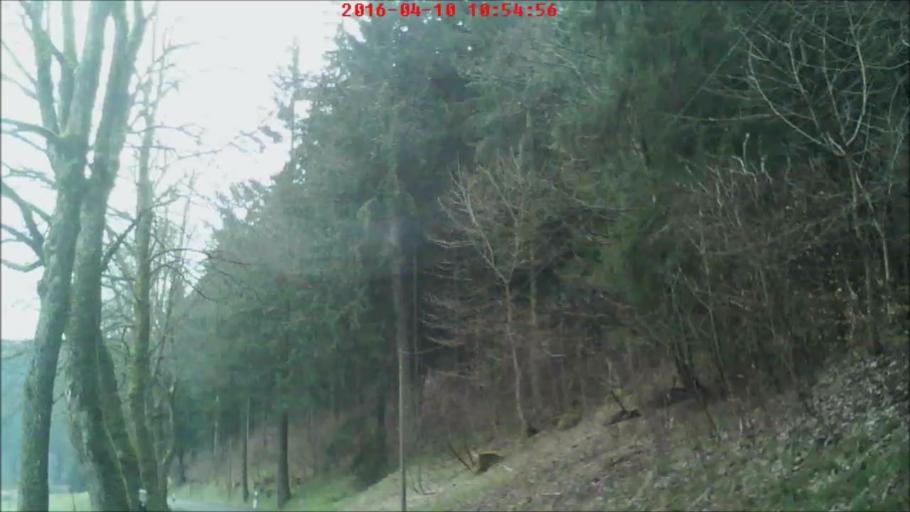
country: DE
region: Thuringia
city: Stutzerbach
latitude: 50.6275
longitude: 10.8573
